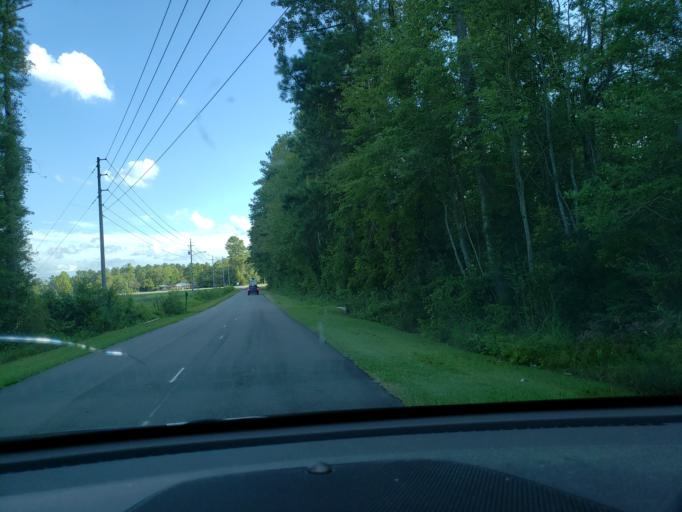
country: US
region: North Carolina
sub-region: Columbus County
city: Tabor City
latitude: 34.1616
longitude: -78.8516
